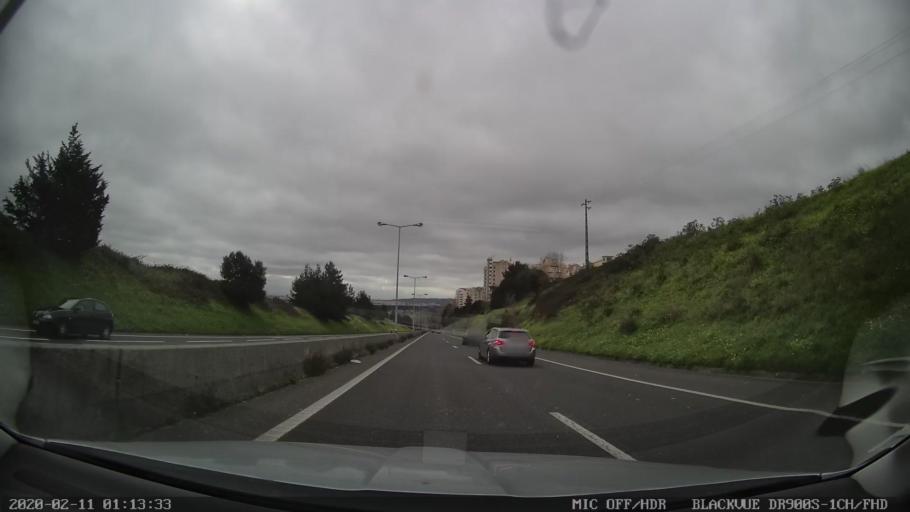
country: PT
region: Lisbon
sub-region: Odivelas
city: Ramada
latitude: 38.8108
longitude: -9.1834
